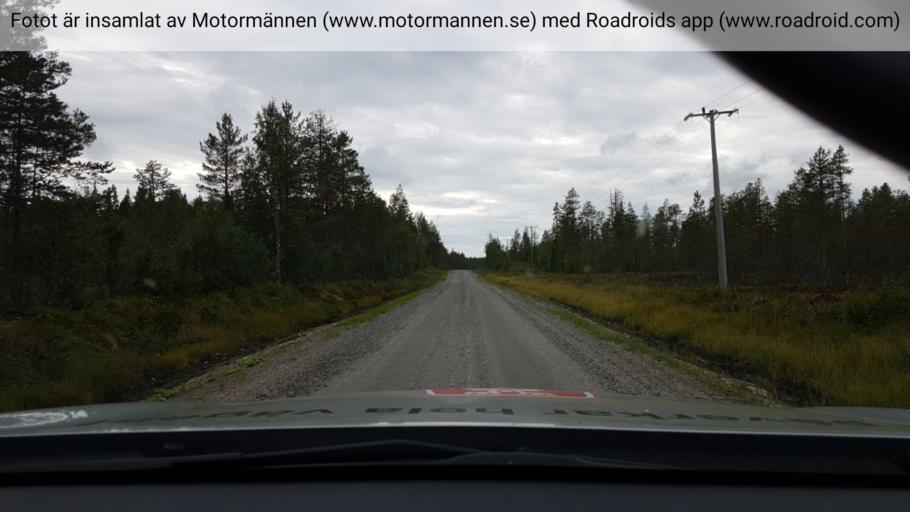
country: SE
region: Vaesterbotten
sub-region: Skelleftea Kommun
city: Langsele
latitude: 64.7325
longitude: 20.2866
